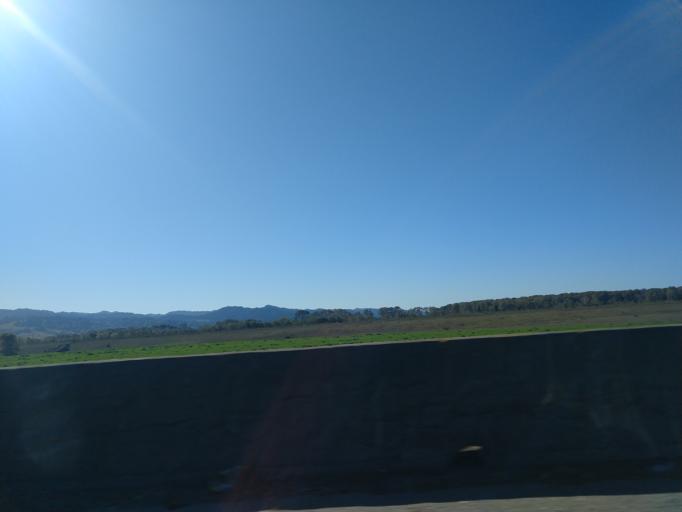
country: US
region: California
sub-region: Humboldt County
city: Fortuna
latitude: 40.5708
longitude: -124.1487
